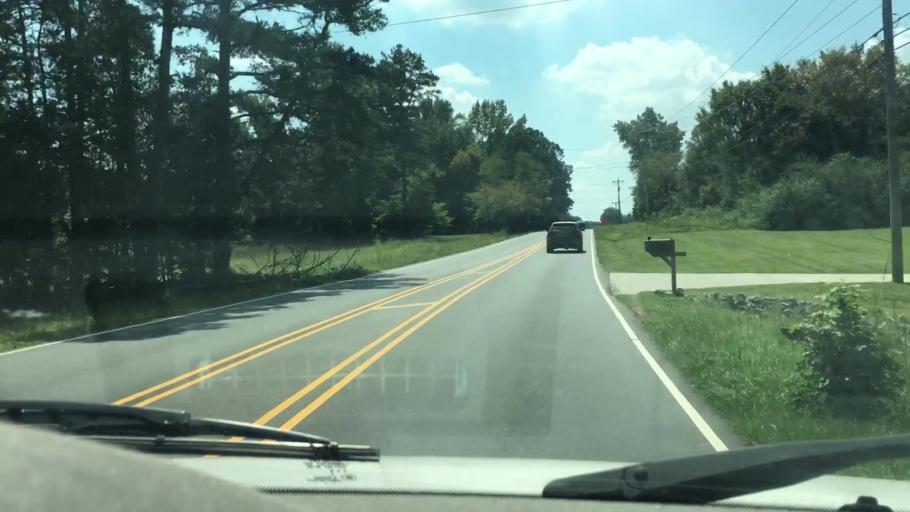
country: US
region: North Carolina
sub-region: Mecklenburg County
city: Huntersville
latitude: 35.3833
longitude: -80.8529
